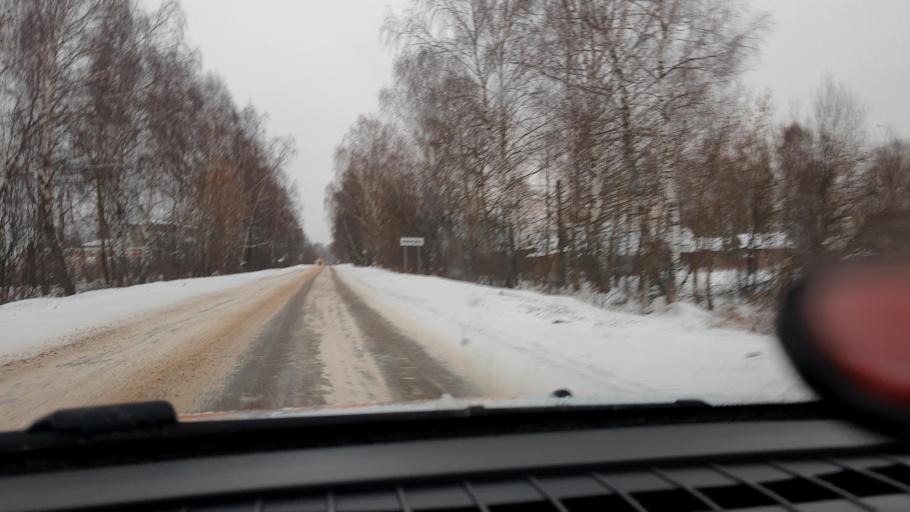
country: RU
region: Nizjnij Novgorod
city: Pamyat' Parizhskoy Kommuny
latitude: 56.2399
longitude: 44.5281
